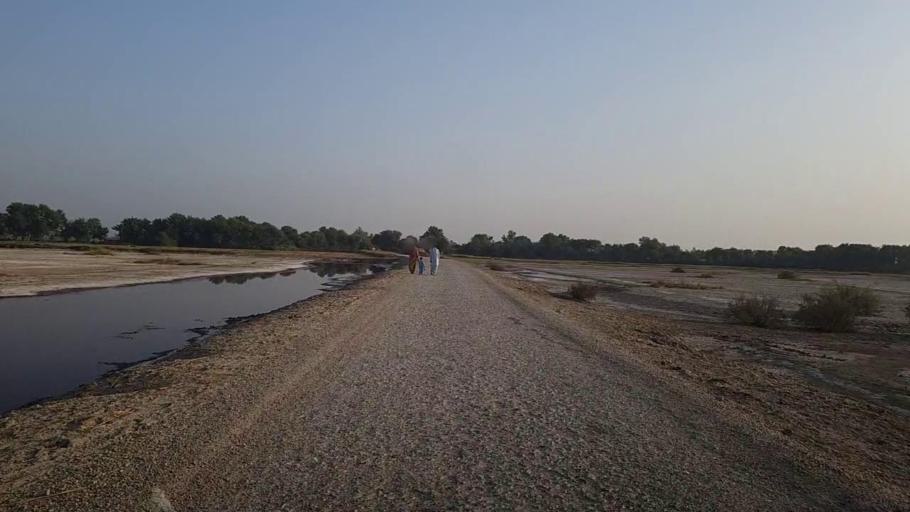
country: PK
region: Sindh
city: Kandhkot
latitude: 28.2437
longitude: 69.0914
